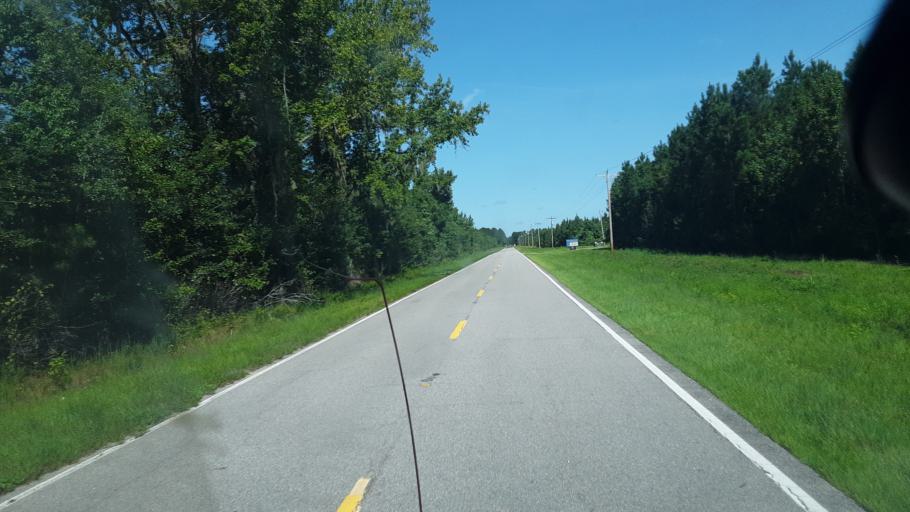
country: US
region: South Carolina
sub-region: Hampton County
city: Varnville
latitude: 32.9387
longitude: -81.0248
